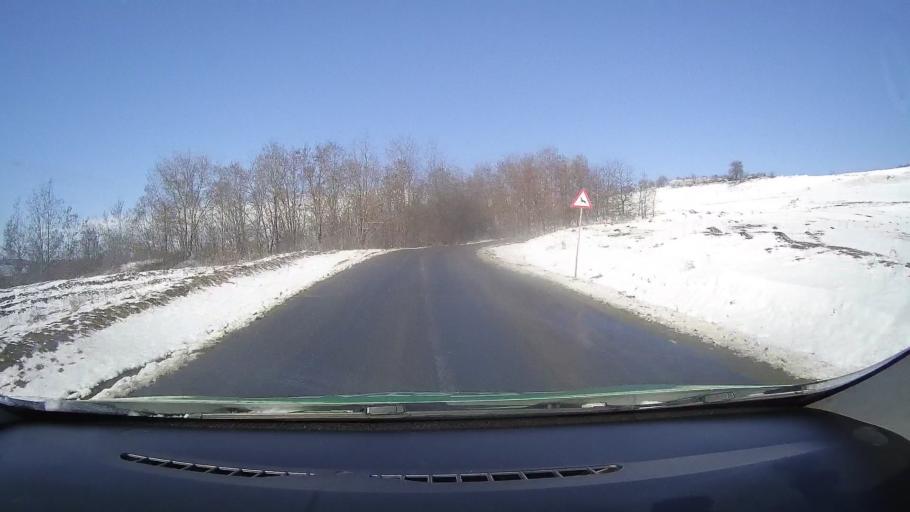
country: RO
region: Sibiu
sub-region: Comuna Rosia
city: Rosia
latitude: 45.8073
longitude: 24.2915
